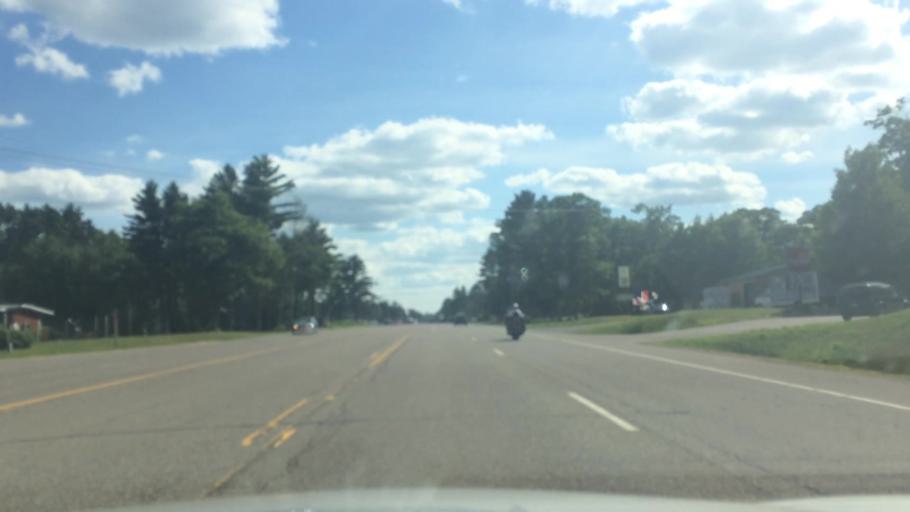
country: US
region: Wisconsin
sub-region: Vilas County
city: Lac du Flambeau
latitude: 45.8343
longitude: -89.7128
